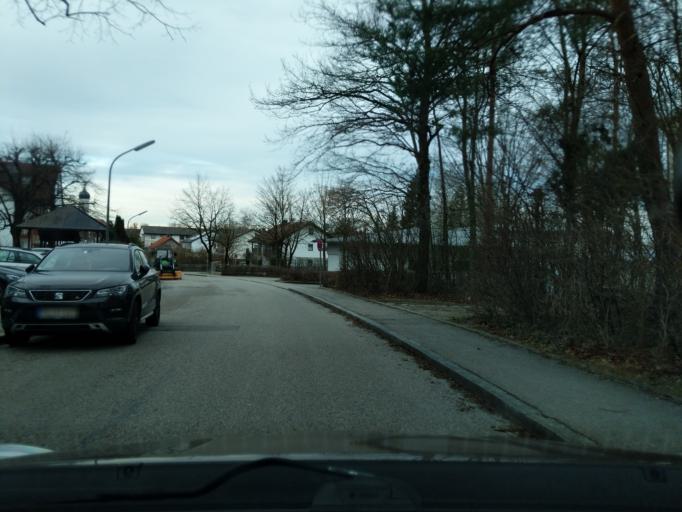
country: DE
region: Bavaria
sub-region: Upper Bavaria
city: Zorneding
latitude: 48.0838
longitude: 11.8286
